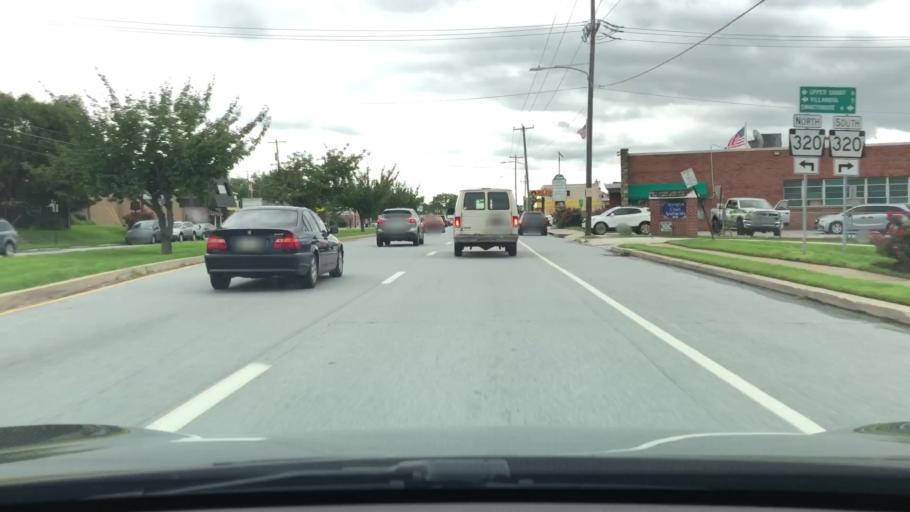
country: US
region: Pennsylvania
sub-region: Delaware County
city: Broomall
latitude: 39.9820
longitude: -75.3633
